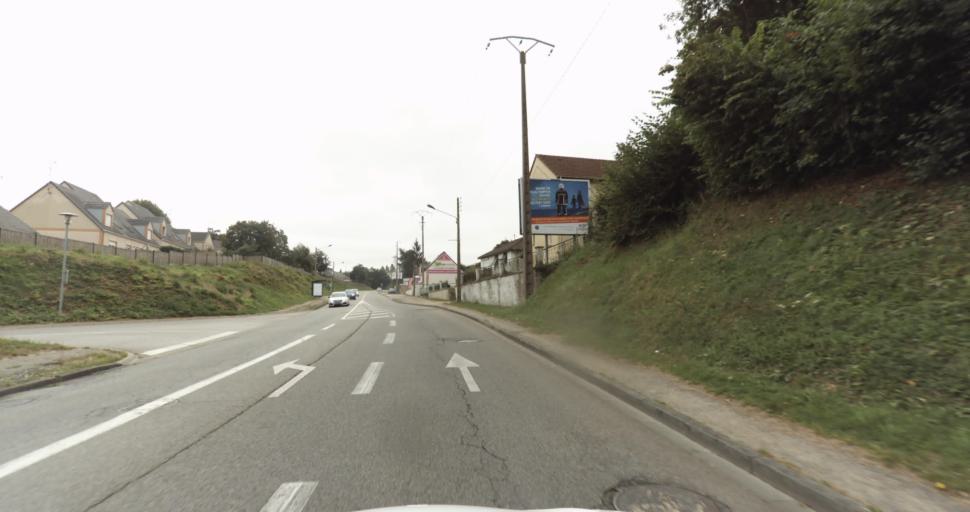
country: FR
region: Haute-Normandie
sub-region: Departement de l'Eure
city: Evreux
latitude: 49.0252
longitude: 1.1670
